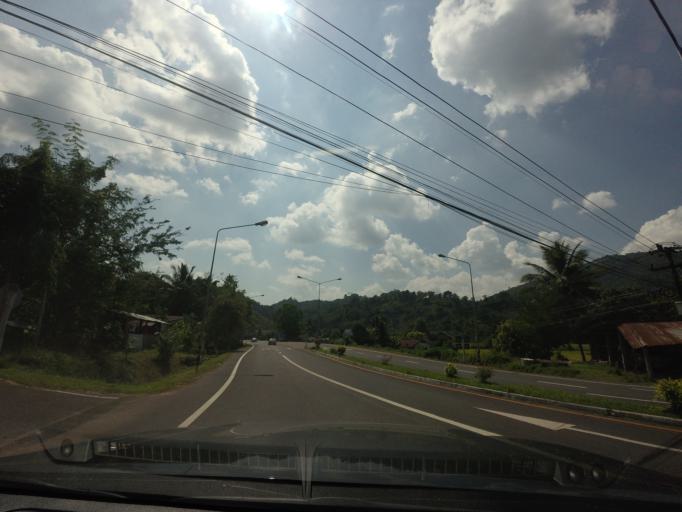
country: TH
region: Nan
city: Bo Kluea
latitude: 19.0816
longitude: 101.1533
